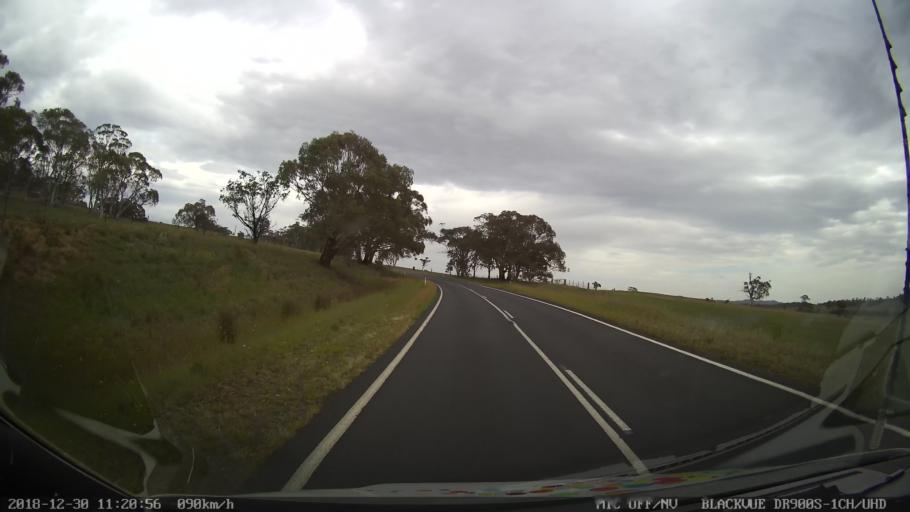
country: AU
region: New South Wales
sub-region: Snowy River
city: Jindabyne
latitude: -36.5123
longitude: 148.6859
